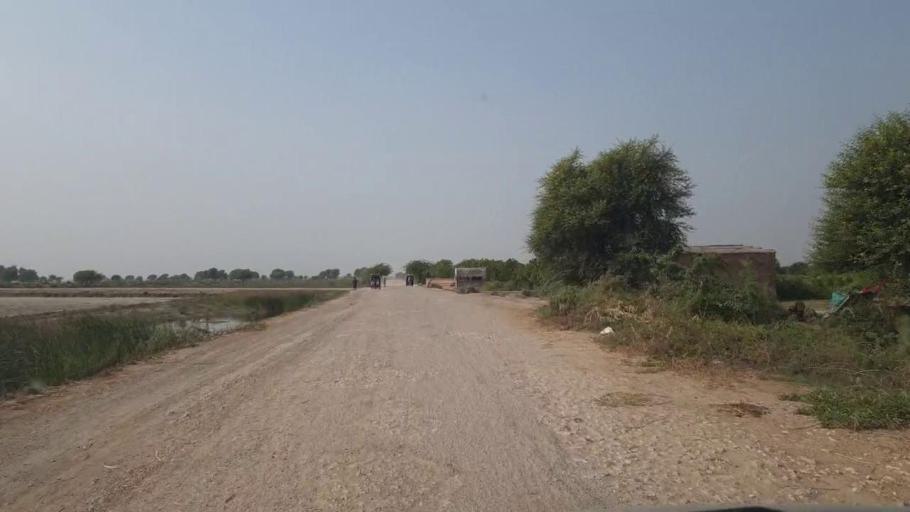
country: PK
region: Sindh
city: Matli
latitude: 25.0209
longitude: 68.6841
